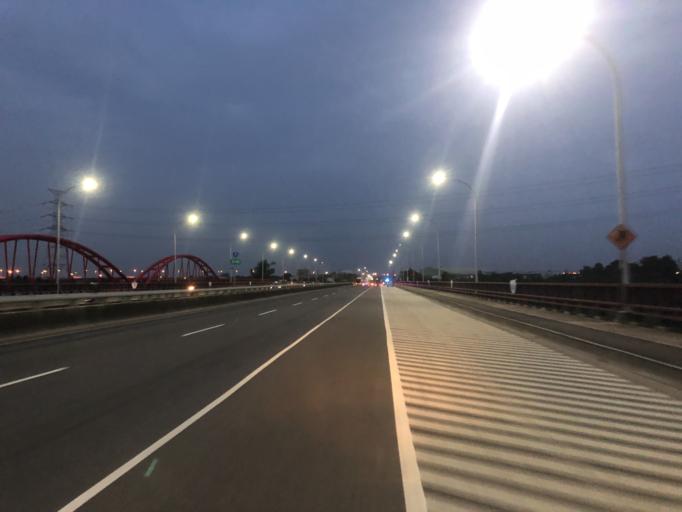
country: TW
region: Taiwan
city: Yujing
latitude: 23.1546
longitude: 120.3374
